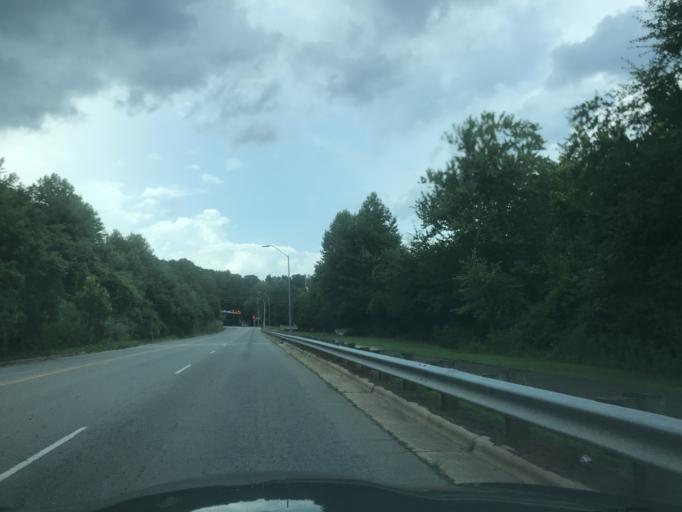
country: US
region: North Carolina
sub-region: Wake County
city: West Raleigh
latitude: 35.8398
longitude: -78.6823
